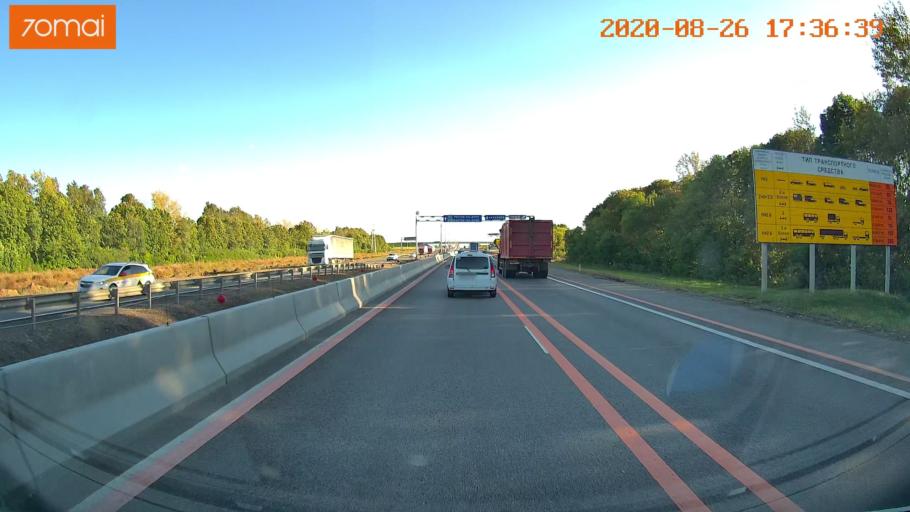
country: RU
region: Tula
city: Kazachka
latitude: 53.3691
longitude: 38.1833
